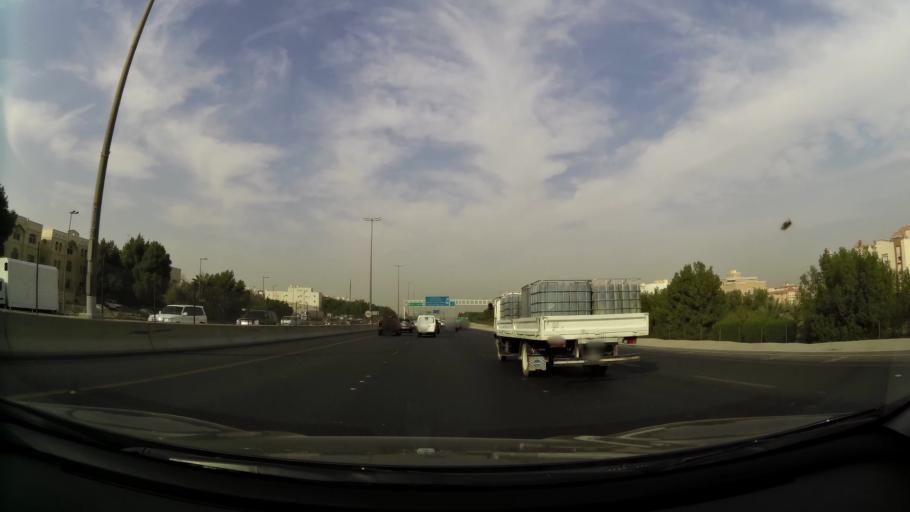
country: KW
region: Al Farwaniyah
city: Al Farwaniyah
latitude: 29.2670
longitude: 47.9350
